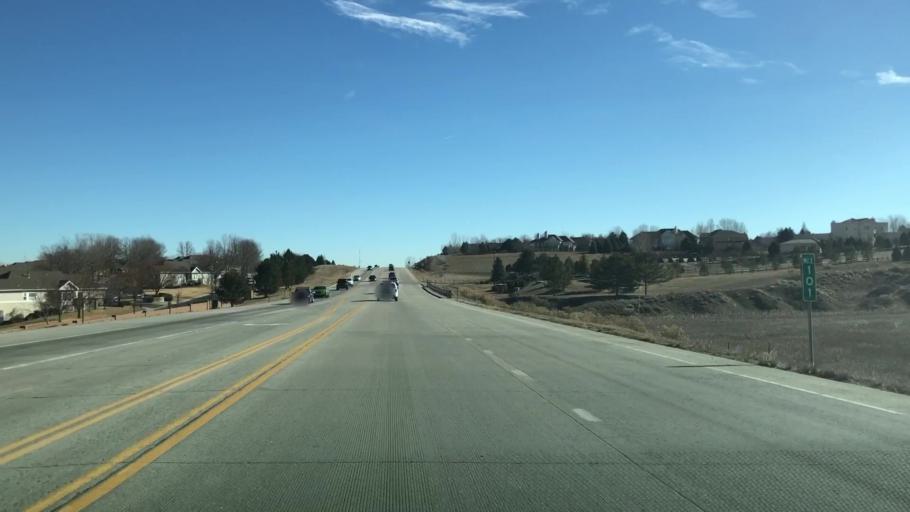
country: US
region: Colorado
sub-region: Weld County
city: Windsor
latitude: 40.4793
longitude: -104.9722
